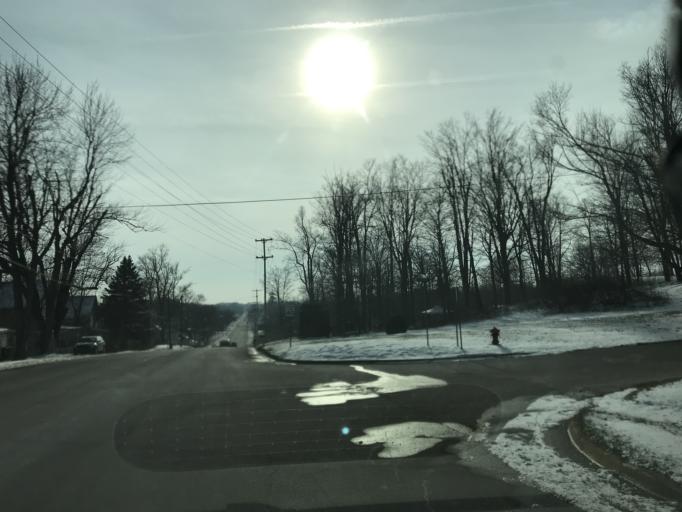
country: US
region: Michigan
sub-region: Barry County
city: Nashville
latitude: 42.6108
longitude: -85.0934
